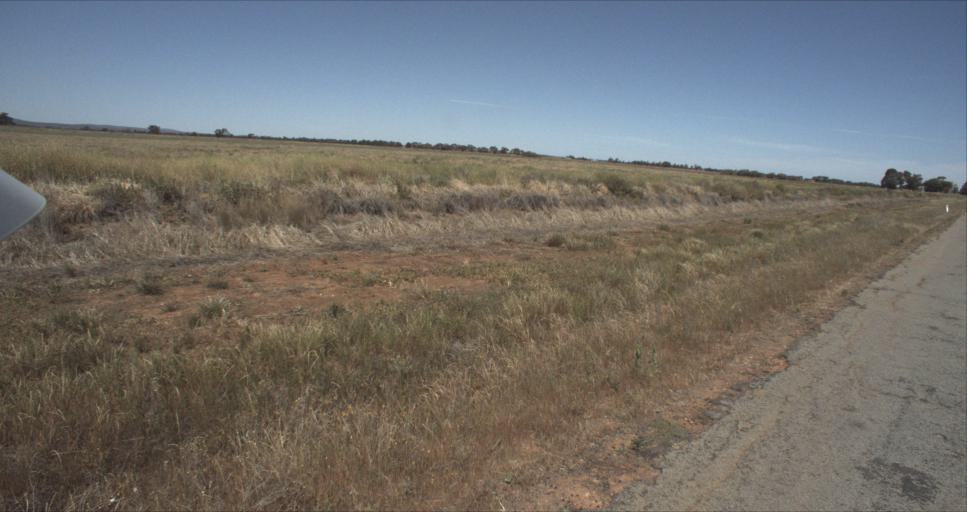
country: AU
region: New South Wales
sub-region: Leeton
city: Leeton
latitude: -34.5059
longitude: 146.3444
